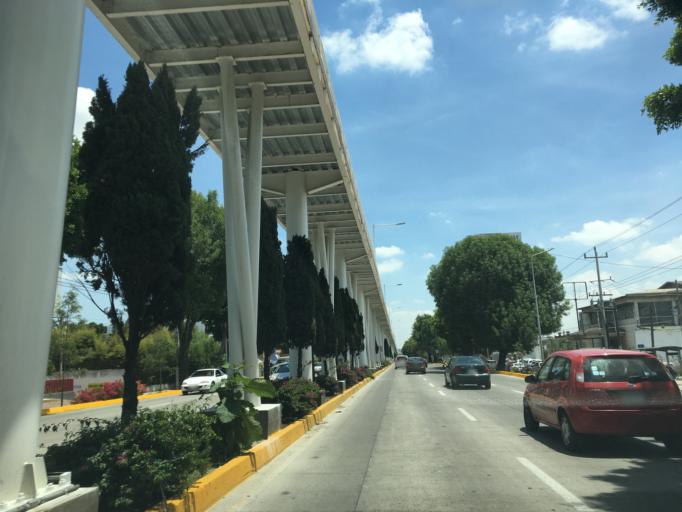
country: MX
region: Puebla
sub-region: Cuautlancingo
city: Sanctorum
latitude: 19.0842
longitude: -98.2287
